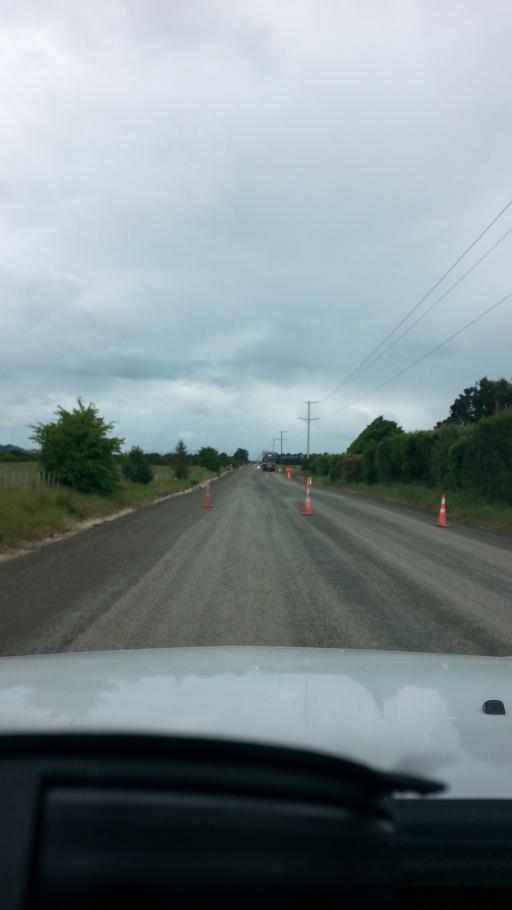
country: NZ
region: Wellington
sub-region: Masterton District
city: Masterton
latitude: -40.8271
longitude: 175.6258
